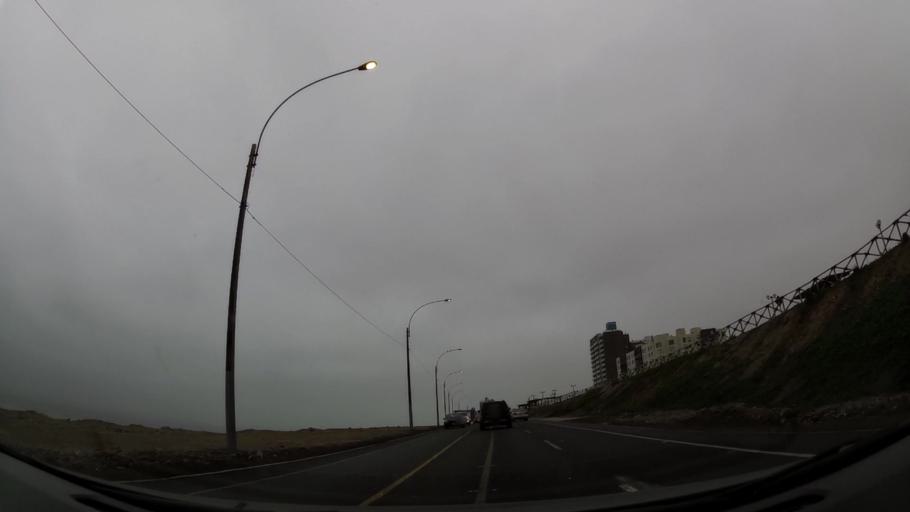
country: PE
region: Callao
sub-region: Callao
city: Callao
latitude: -12.0878
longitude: -77.0928
